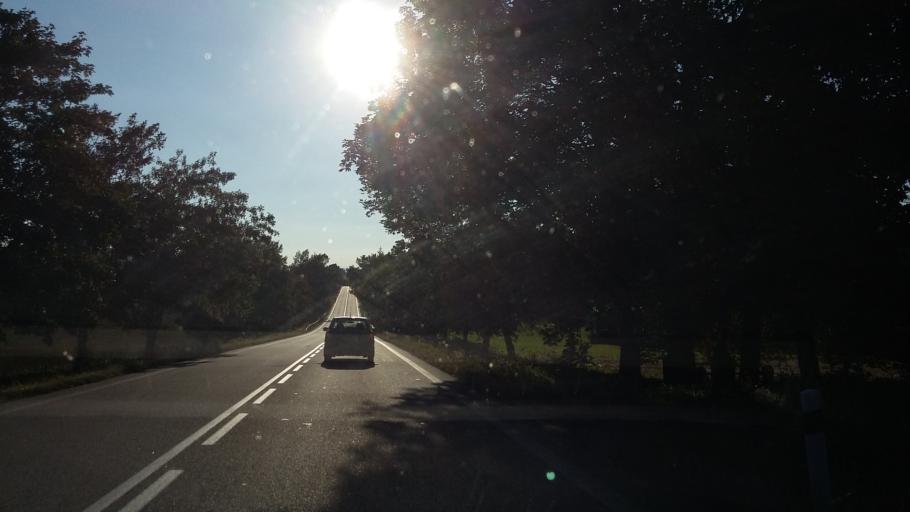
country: CZ
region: Vysocina
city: Kamenice
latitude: 49.3970
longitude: 15.7578
